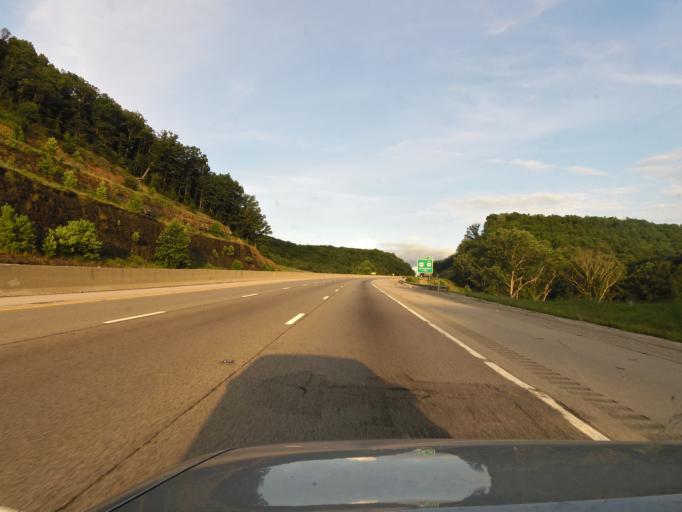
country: US
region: Kentucky
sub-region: Rockcastle County
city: Mount Vernon
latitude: 37.2365
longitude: -84.2330
